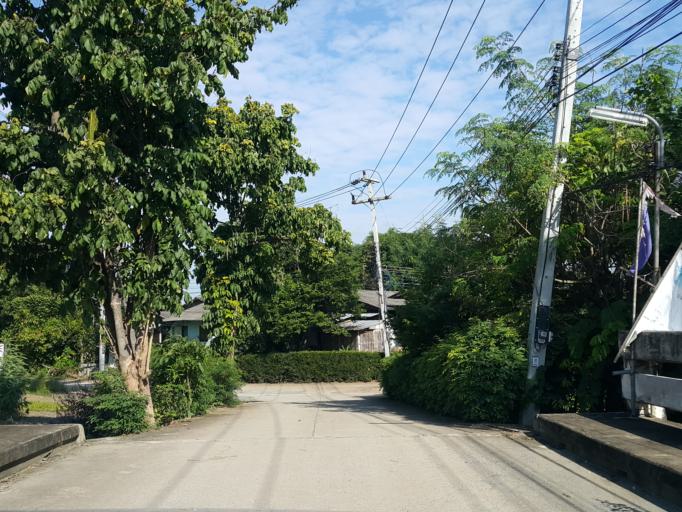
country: TH
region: Chiang Mai
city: Mae On
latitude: 18.8223
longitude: 99.1700
